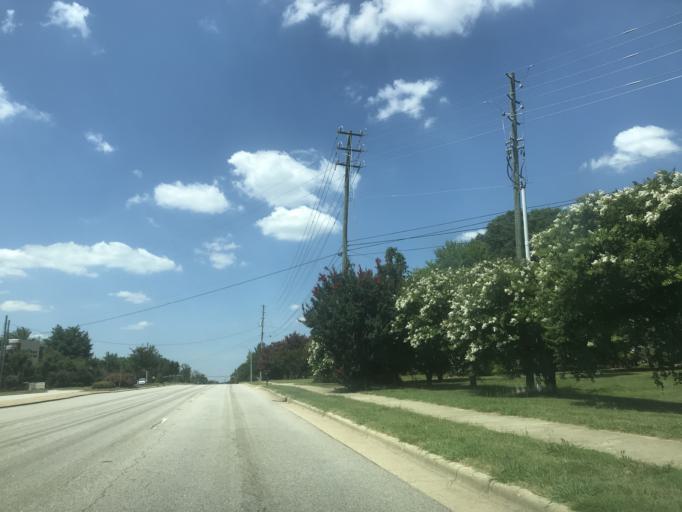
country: US
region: North Carolina
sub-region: Wake County
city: Cary
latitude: 35.7506
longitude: -78.7409
